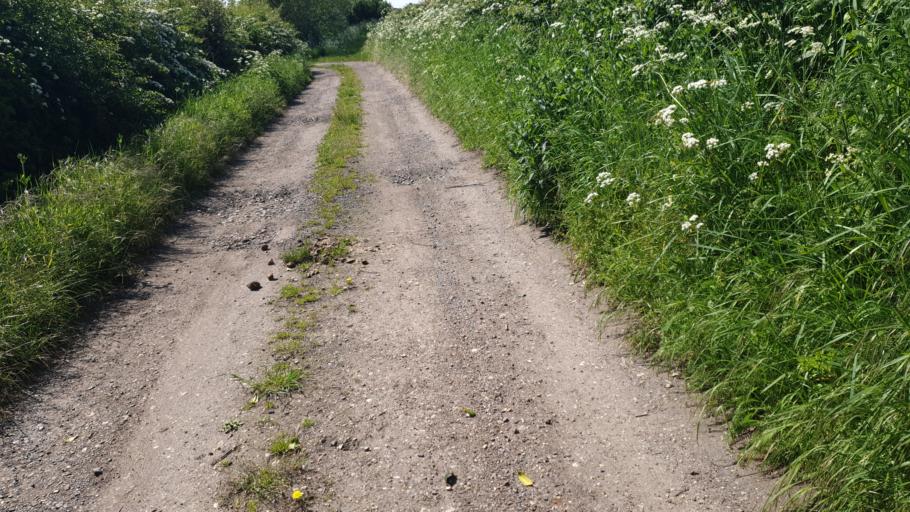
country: GB
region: England
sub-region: Essex
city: Manningtree
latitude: 51.9307
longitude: 1.0413
